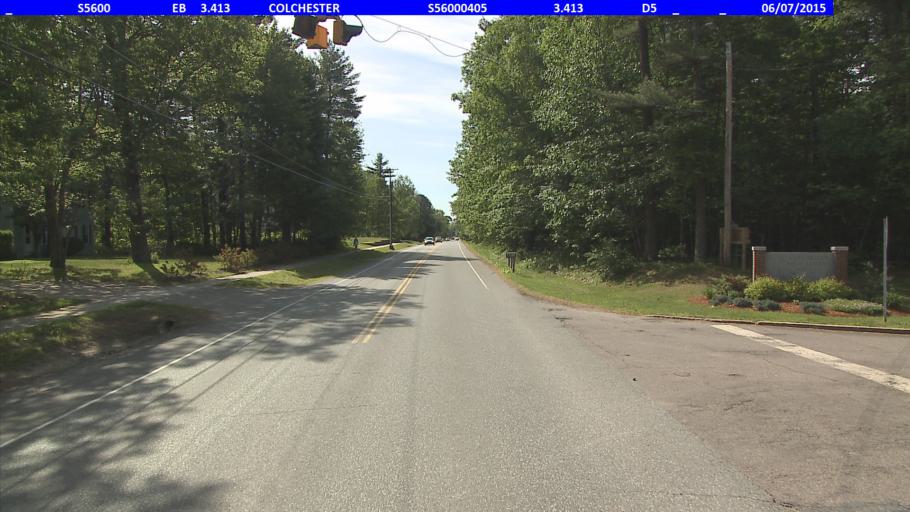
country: US
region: Vermont
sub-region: Chittenden County
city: Winooski
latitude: 44.5422
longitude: -73.2130
